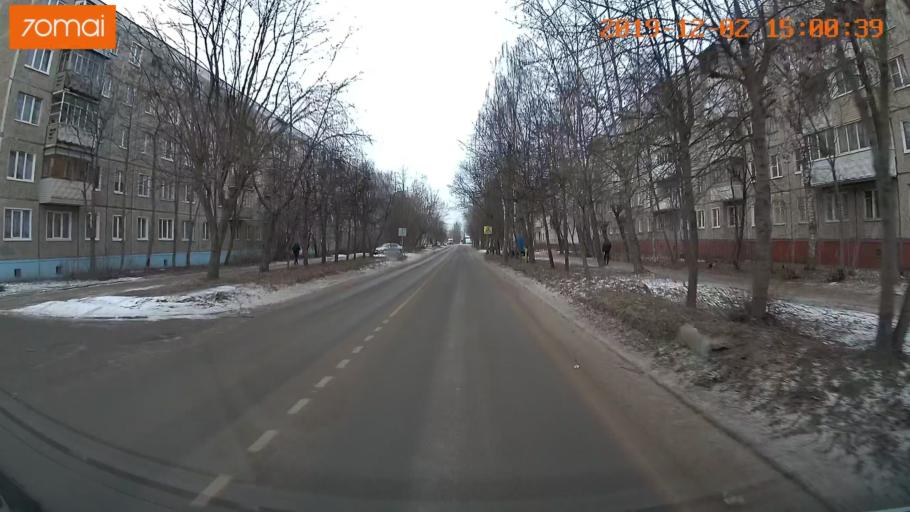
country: RU
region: Ivanovo
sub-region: Gorod Ivanovo
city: Ivanovo
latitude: 56.9714
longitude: 41.0027
